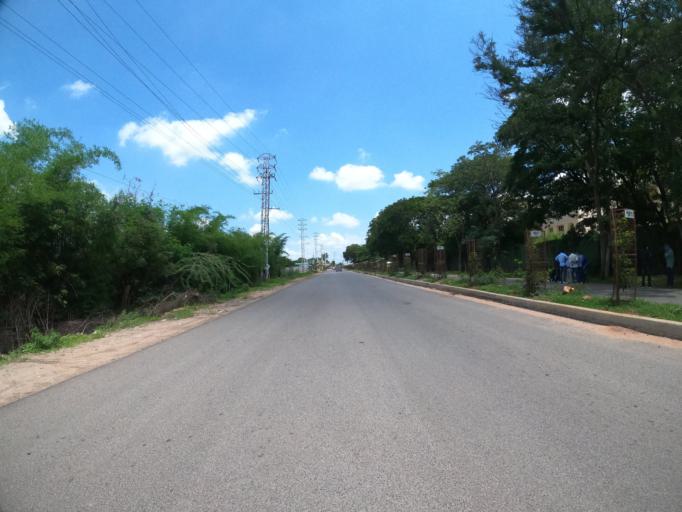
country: IN
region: Telangana
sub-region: Rangareddi
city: Singapur
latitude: 17.4186
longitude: 78.2204
